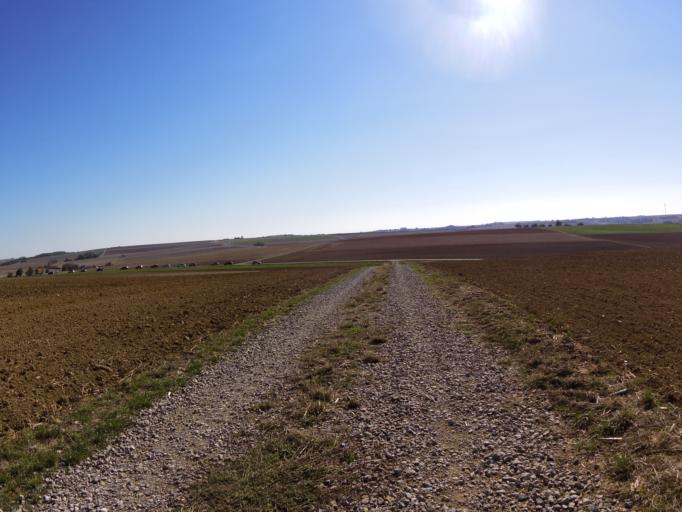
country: DE
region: Bavaria
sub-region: Regierungsbezirk Unterfranken
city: Reichenberg
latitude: 49.7338
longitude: 9.9286
